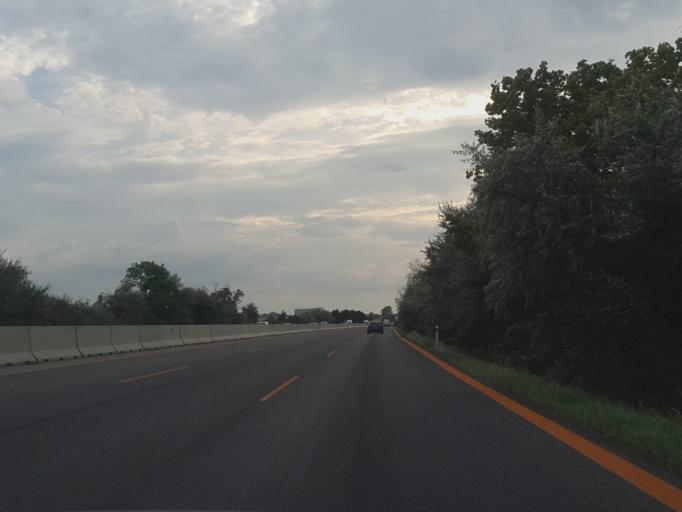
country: SK
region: Bratislavsky
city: Senec
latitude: 48.2483
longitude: 17.4203
